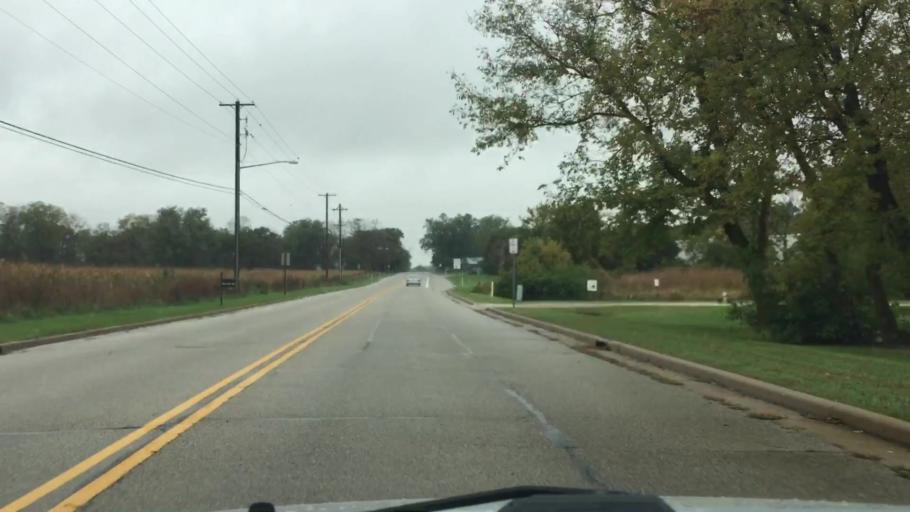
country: US
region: Wisconsin
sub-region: Jefferson County
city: Palmyra
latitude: 42.8786
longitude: -88.5998
